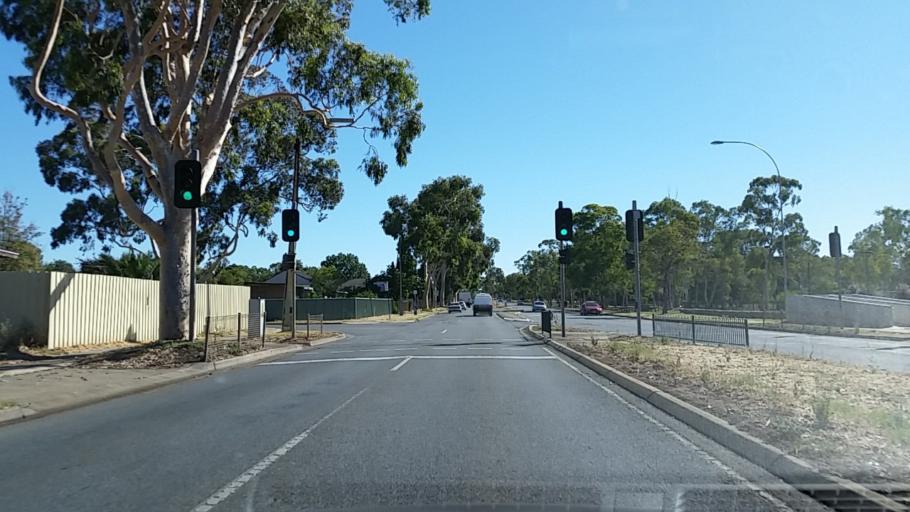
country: AU
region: South Australia
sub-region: Salisbury
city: Ingle Farm
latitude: -34.8102
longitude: 138.6462
